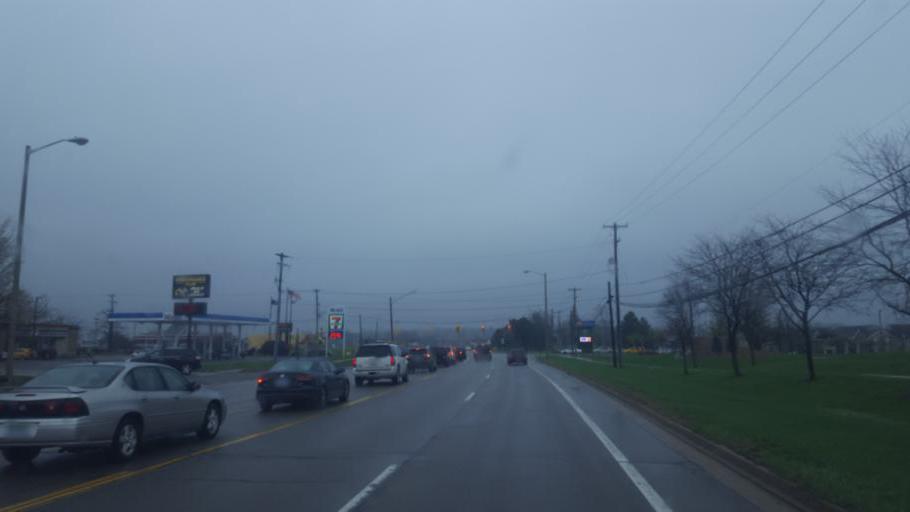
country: US
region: Michigan
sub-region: Isabella County
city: Mount Pleasant
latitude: 43.5767
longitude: -84.7675
